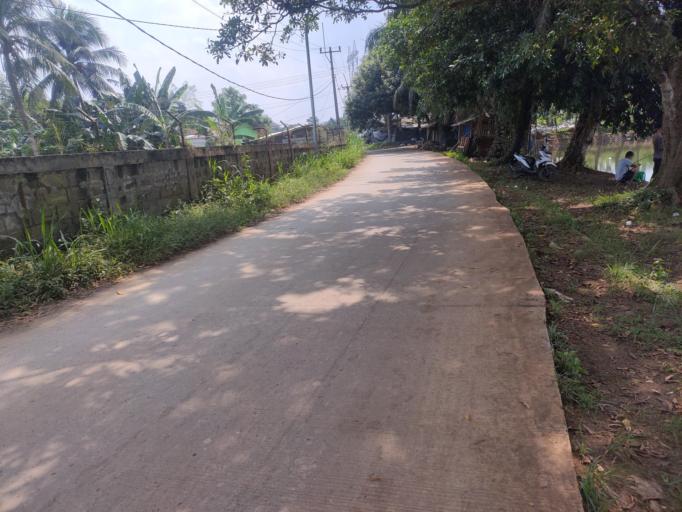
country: ID
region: West Java
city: Parung
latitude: -6.4582
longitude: 106.7078
